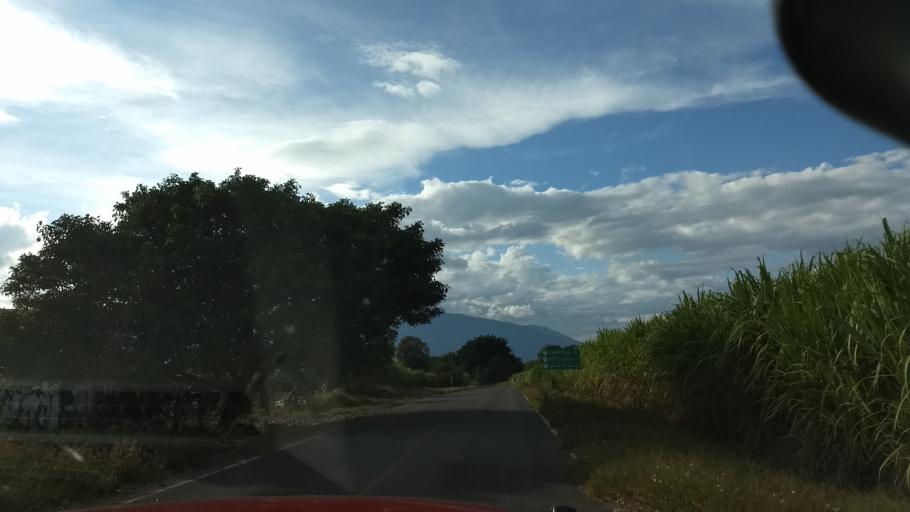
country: MX
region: Colima
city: Suchitlan
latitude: 19.4673
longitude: -103.7626
